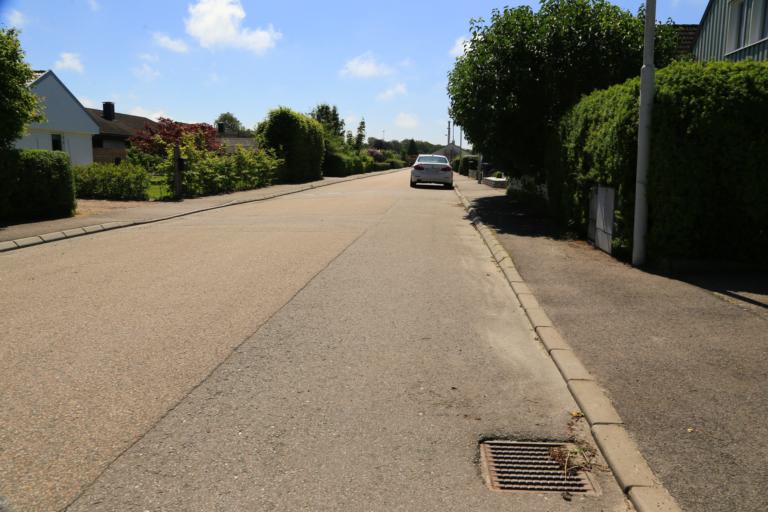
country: SE
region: Halland
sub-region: Varbergs Kommun
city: Varberg
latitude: 57.1074
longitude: 12.2768
